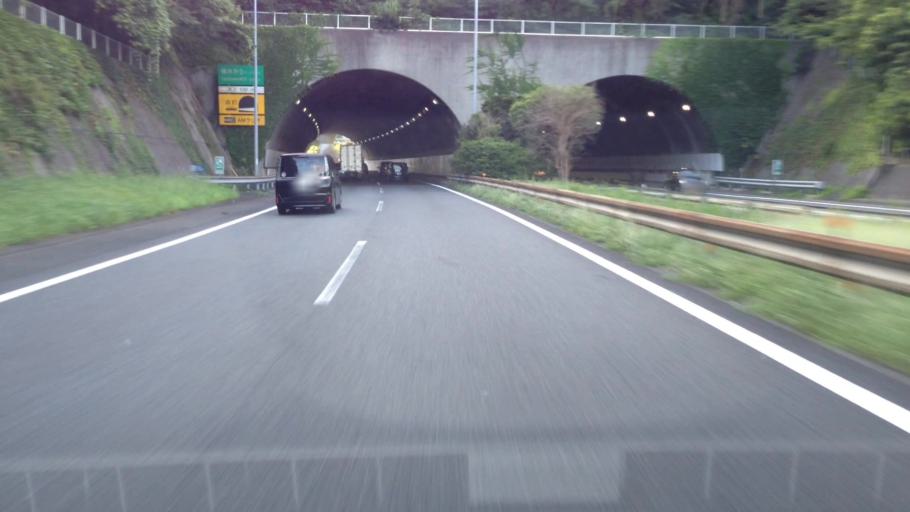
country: JP
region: Kanagawa
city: Zushi
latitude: 35.3223
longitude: 139.6028
